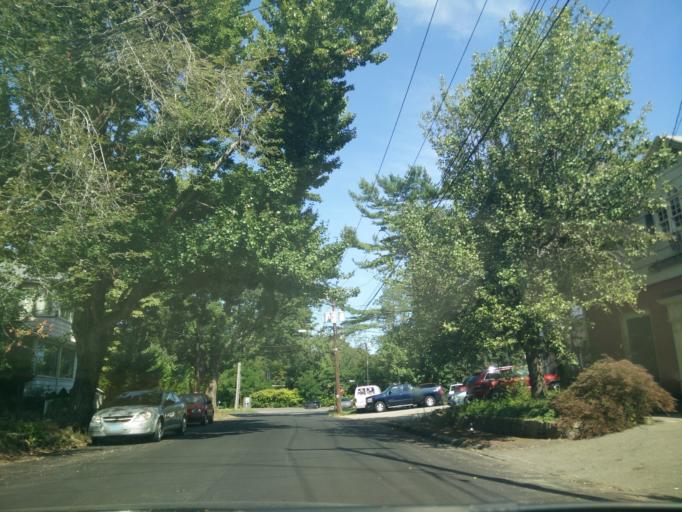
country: US
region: Connecticut
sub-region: Fairfield County
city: Bridgeport
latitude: 41.1657
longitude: -73.2310
